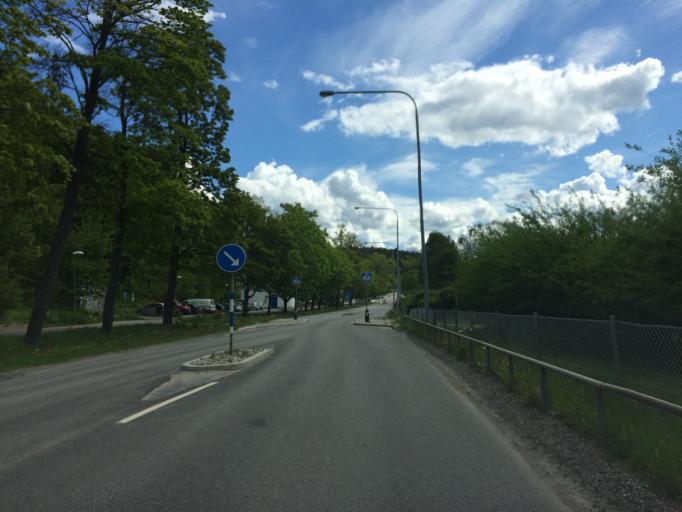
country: SE
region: Stockholm
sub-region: Botkyrka Kommun
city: Fittja
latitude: 59.2593
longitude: 17.8797
